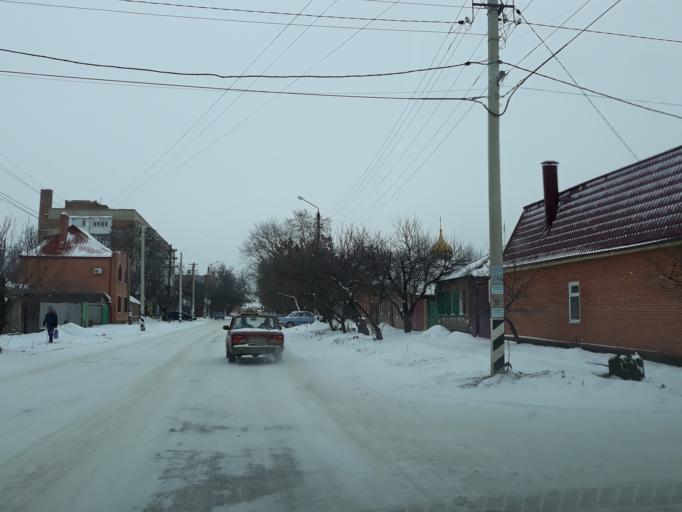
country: RU
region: Rostov
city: Taganrog
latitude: 47.2329
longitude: 38.8804
